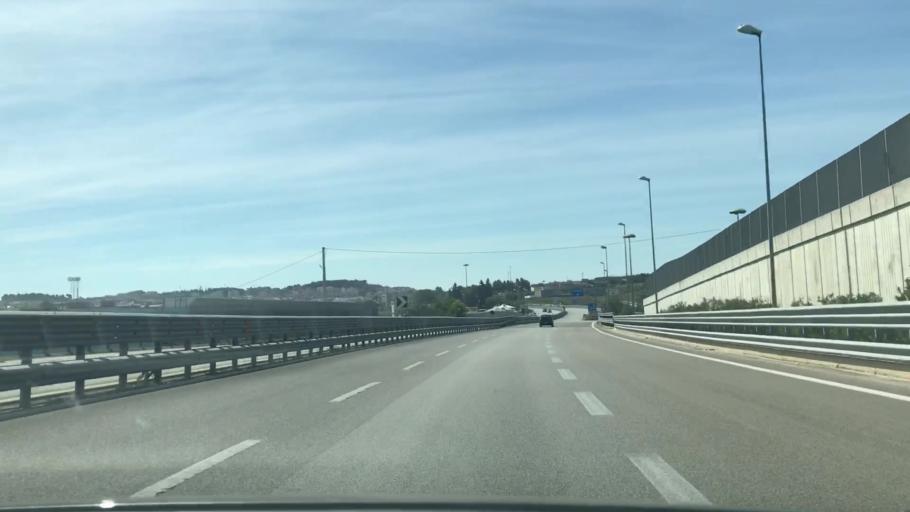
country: IT
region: Basilicate
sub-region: Provincia di Matera
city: Matera
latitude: 40.6925
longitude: 16.5915
